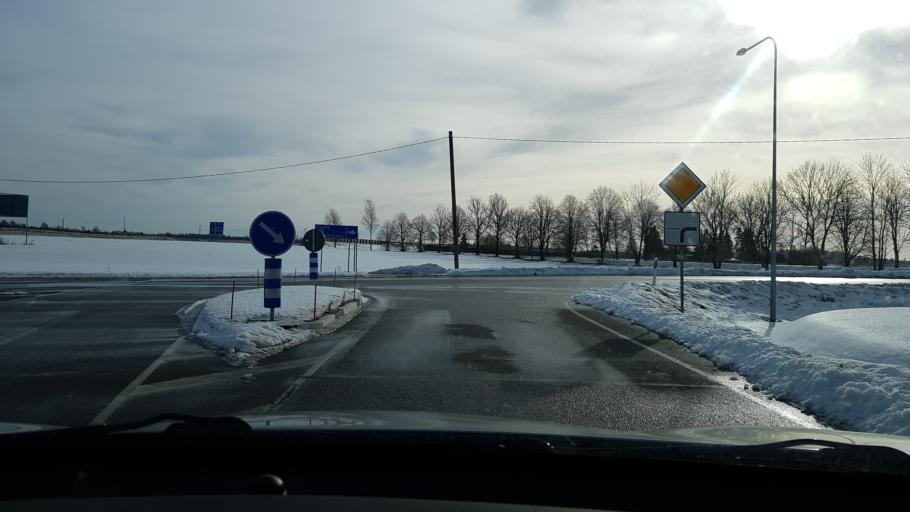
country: EE
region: Jaervamaa
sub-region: Paide linn
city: Paide
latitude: 58.9309
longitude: 25.6080
